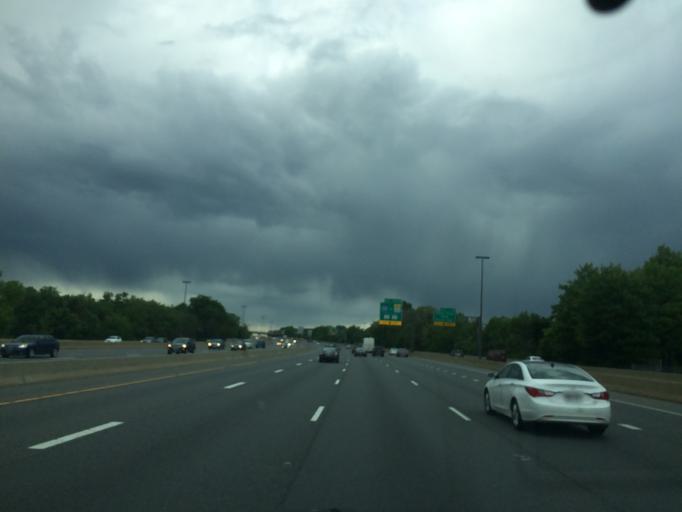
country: US
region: Maryland
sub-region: Montgomery County
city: Derwood
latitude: 39.1024
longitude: -77.1800
